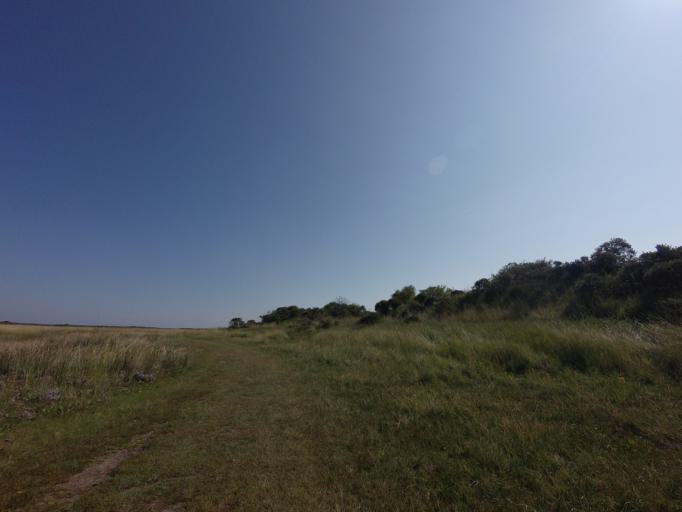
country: NL
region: Friesland
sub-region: Gemeente Schiermonnikoog
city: Schiermonnikoog
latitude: 53.4890
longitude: 6.2242
